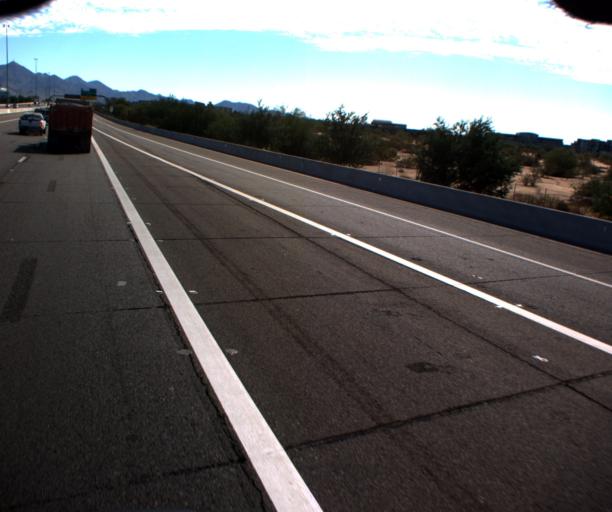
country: US
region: Arizona
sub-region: Maricopa County
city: Paradise Valley
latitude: 33.6609
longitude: -111.9389
